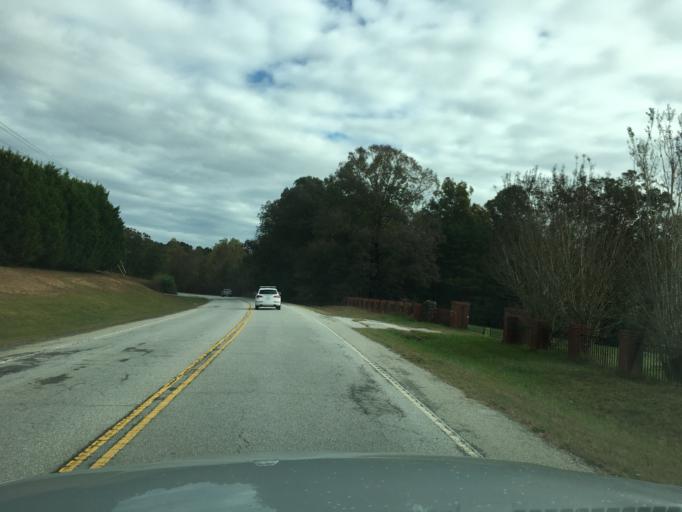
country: US
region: South Carolina
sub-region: Greenville County
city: Tigerville
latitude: 35.0451
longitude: -82.2636
